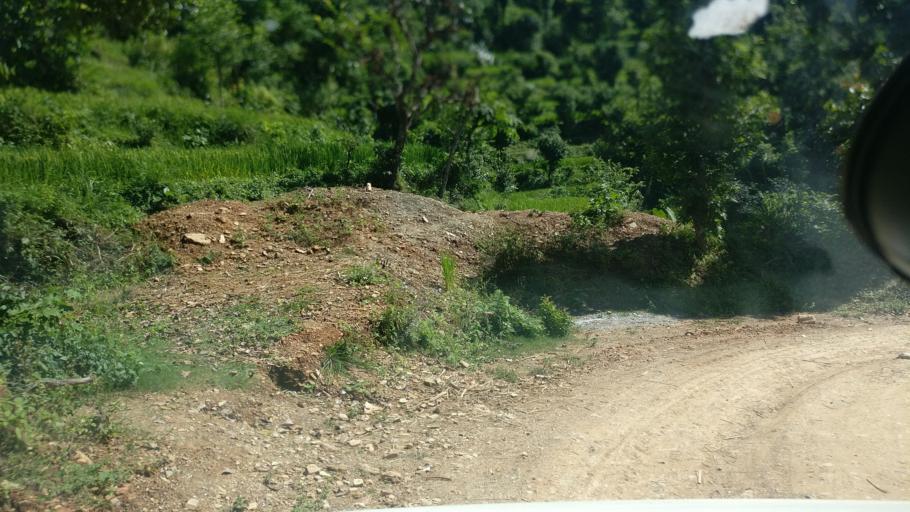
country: NP
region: Western Region
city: Baglung
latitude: 28.1371
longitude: 83.6492
